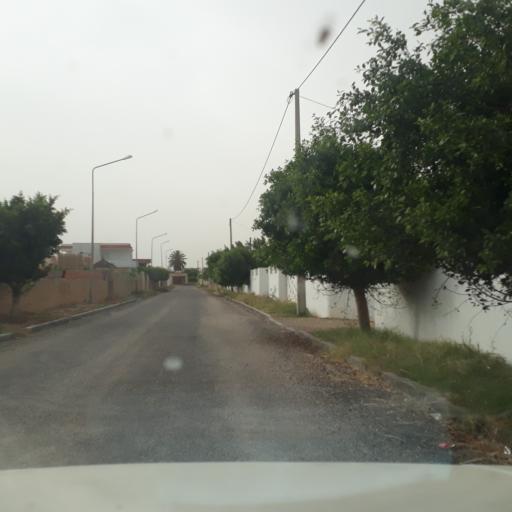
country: TN
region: Safaqis
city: Al Qarmadah
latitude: 34.8125
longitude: 10.7670
